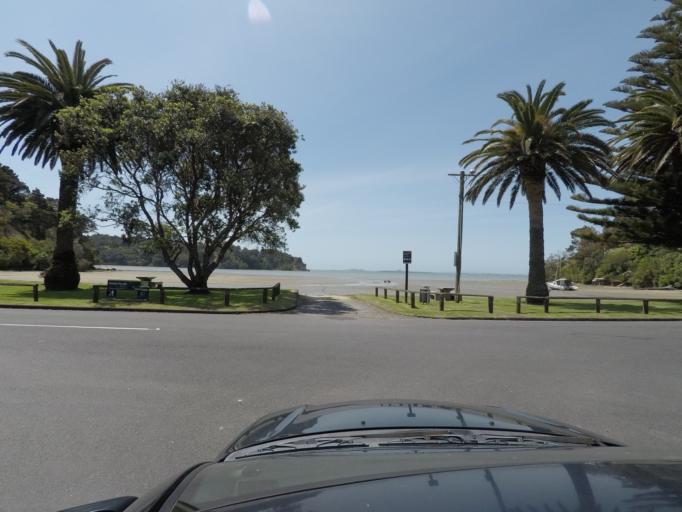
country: NZ
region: Auckland
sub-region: Auckland
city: Titirangi
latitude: -36.9668
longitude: 174.6416
